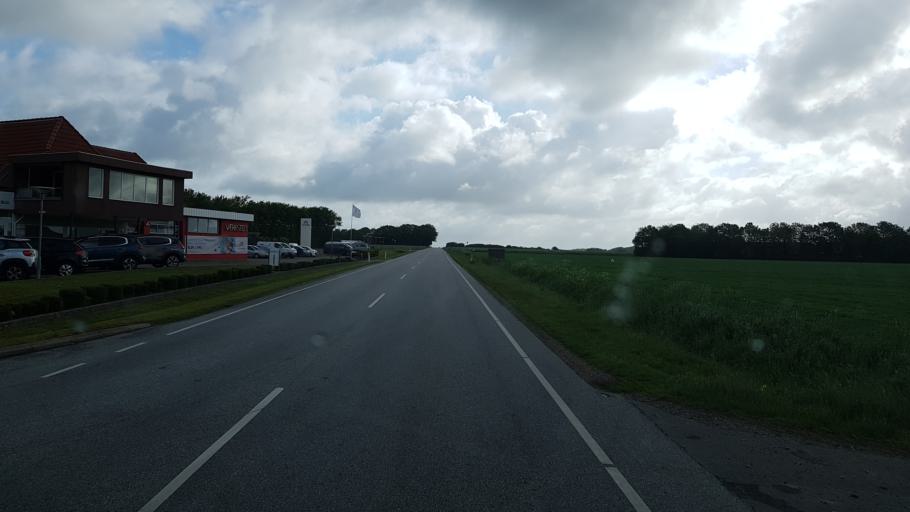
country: DK
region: South Denmark
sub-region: Vejen Kommune
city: Rodding
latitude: 55.3962
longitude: 9.1008
